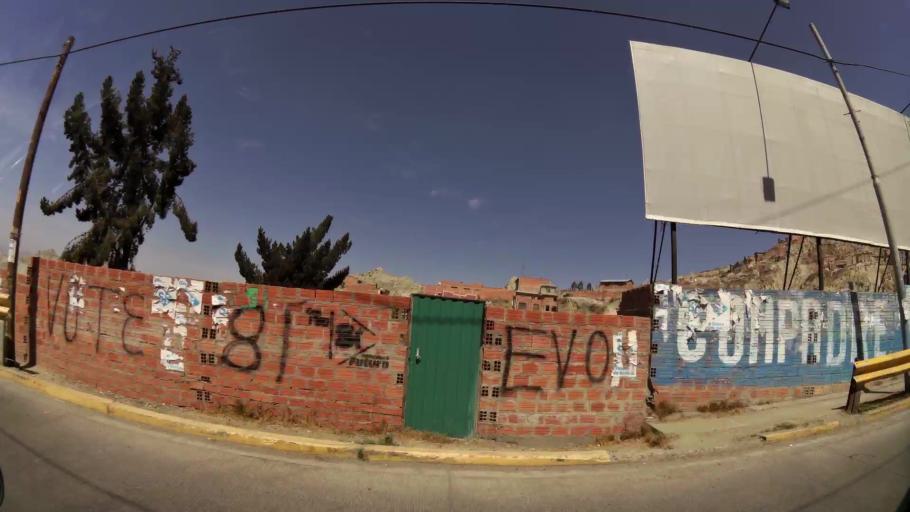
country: BO
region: La Paz
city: La Paz
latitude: -16.5341
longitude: -68.1415
